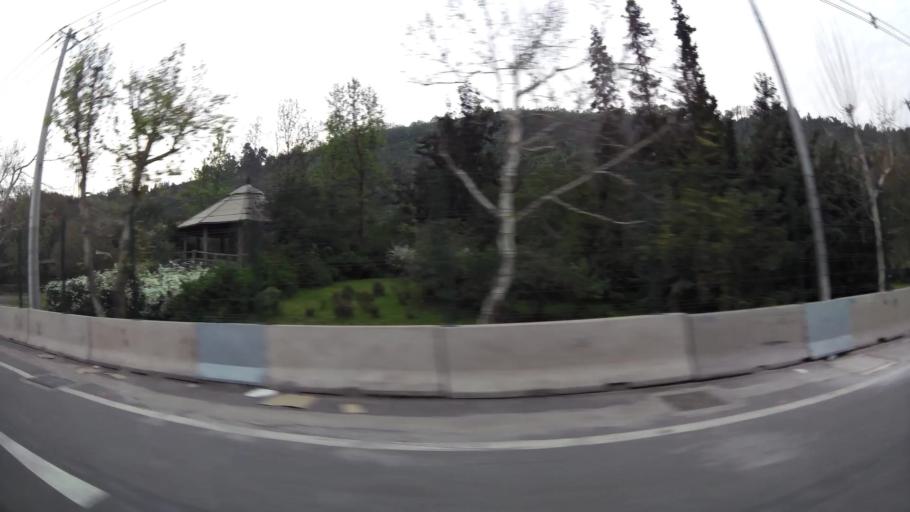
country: CL
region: Santiago Metropolitan
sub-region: Provincia de Santiago
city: Villa Presidente Frei, Nunoa, Santiago, Chile
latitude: -33.4074
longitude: -70.6055
